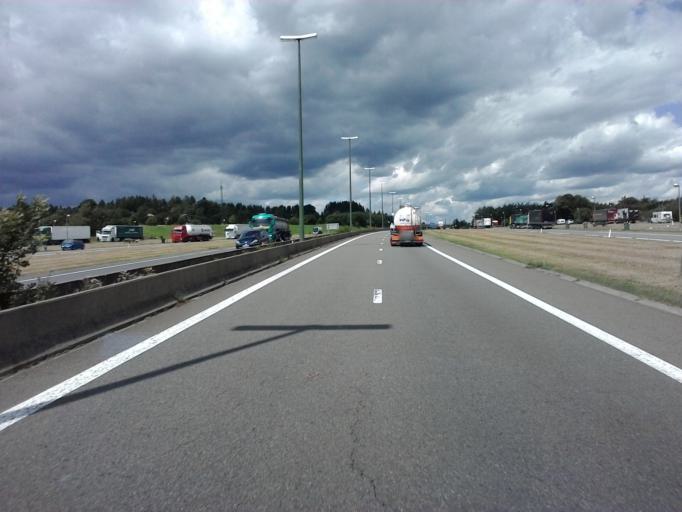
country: BE
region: Wallonia
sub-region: Province du Luxembourg
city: Manhay
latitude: 50.3584
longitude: 5.6755
